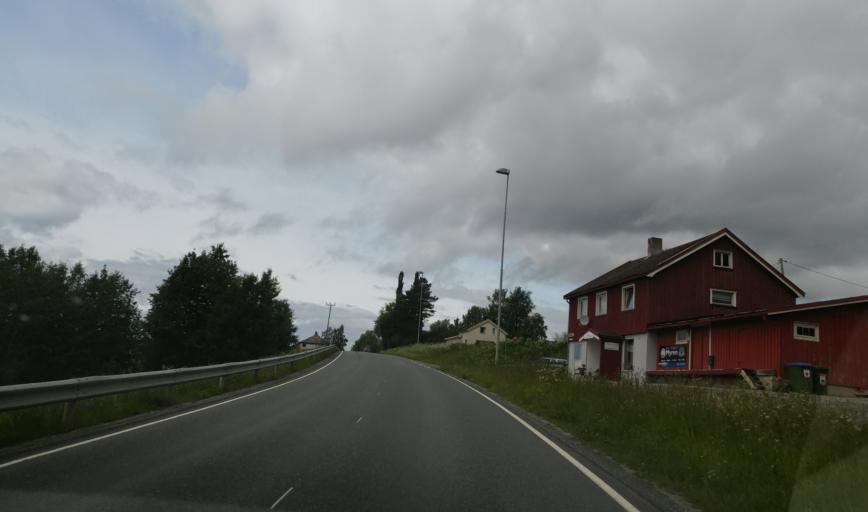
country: NO
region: Nord-Trondelag
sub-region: Stjordal
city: Stjordalshalsen
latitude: 63.3919
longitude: 11.0692
